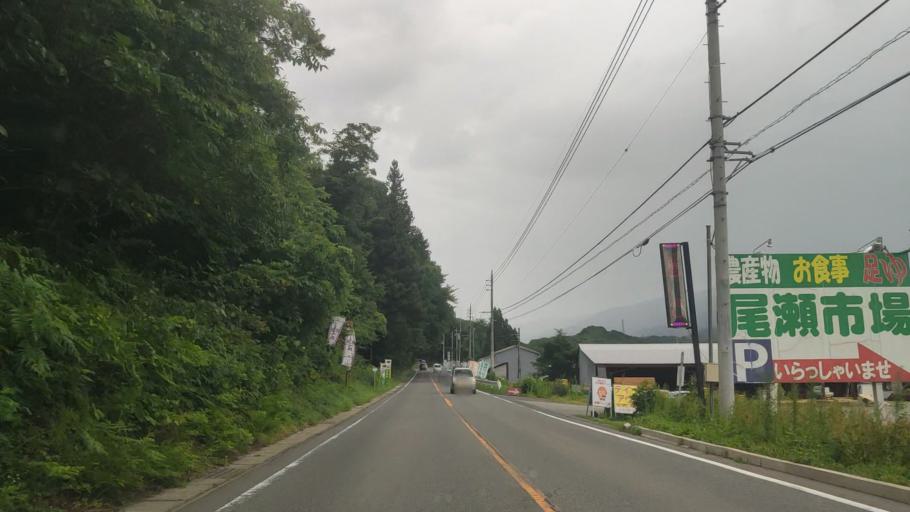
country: JP
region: Gunma
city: Numata
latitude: 36.7154
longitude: 139.2110
